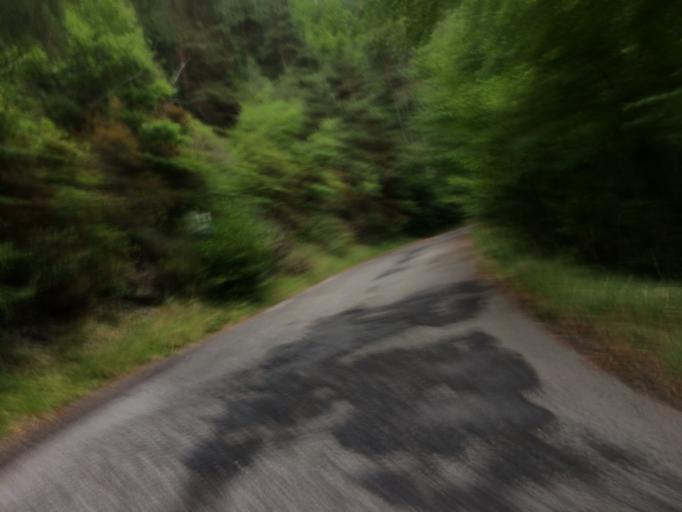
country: IT
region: Liguria
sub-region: Provincia di Imperia
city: Triora
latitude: 43.9741
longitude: 7.7441
